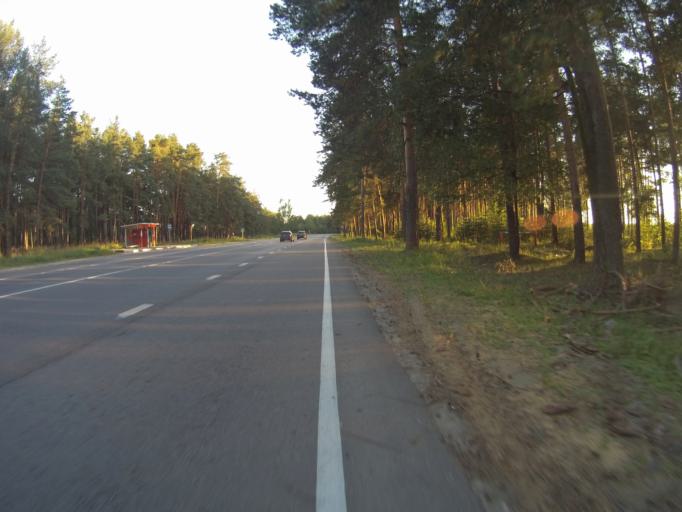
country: RU
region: Vladimir
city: Kommunar
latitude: 56.0404
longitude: 40.4300
